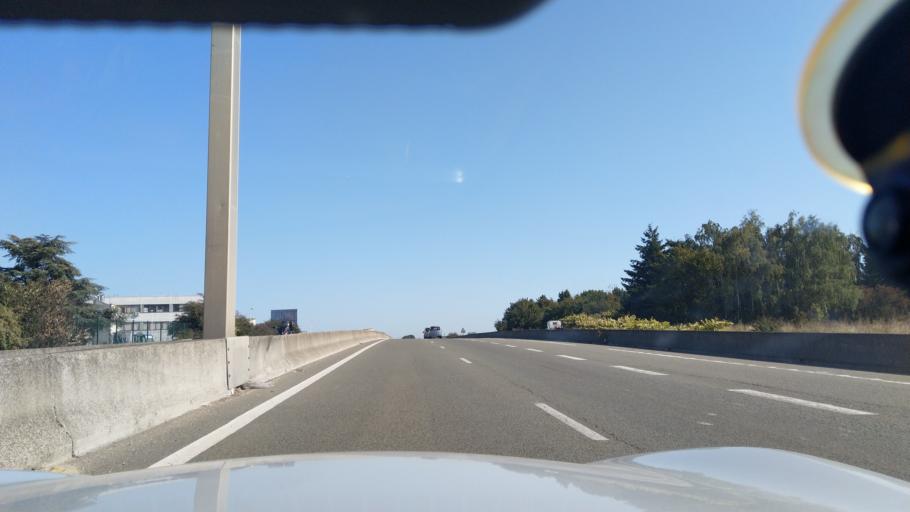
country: FR
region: Ile-de-France
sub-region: Departement du Val-d'Oise
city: Le Thillay
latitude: 48.9956
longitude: 2.4802
